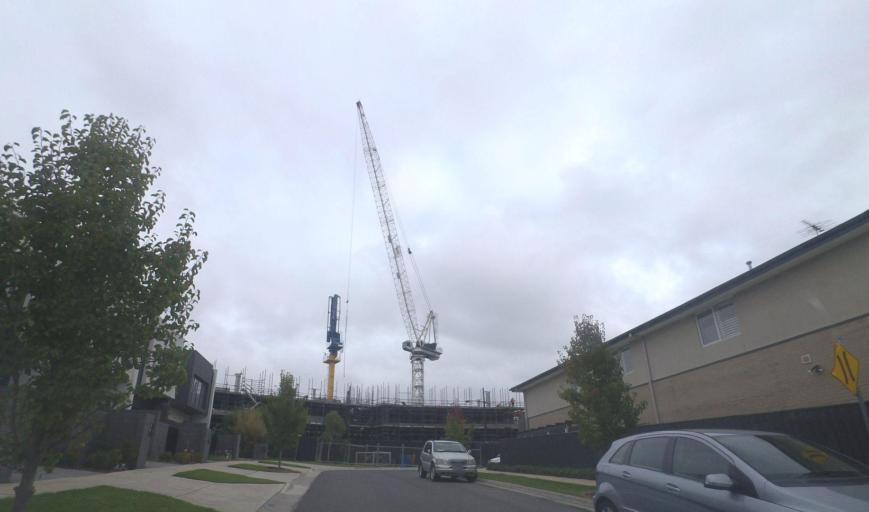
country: AU
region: Victoria
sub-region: Manningham
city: Doncaster
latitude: -37.7869
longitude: 145.1176
